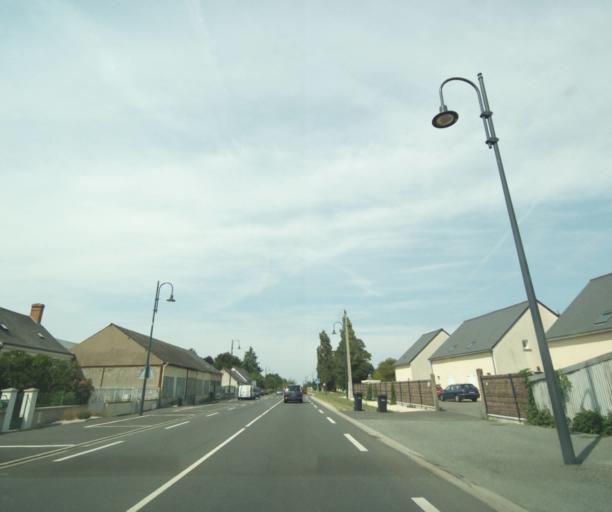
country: FR
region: Centre
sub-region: Departement d'Indre-et-Loire
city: Sorigny
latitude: 47.2443
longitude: 0.6952
